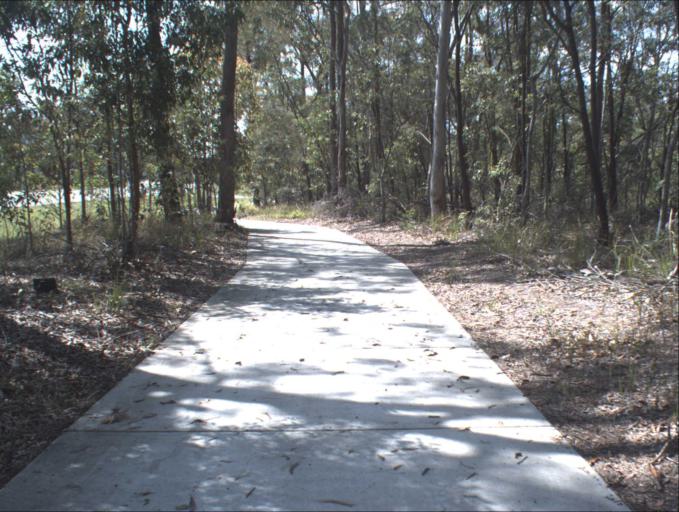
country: AU
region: Queensland
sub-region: Logan
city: Woodridge
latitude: -27.6550
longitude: 153.0676
